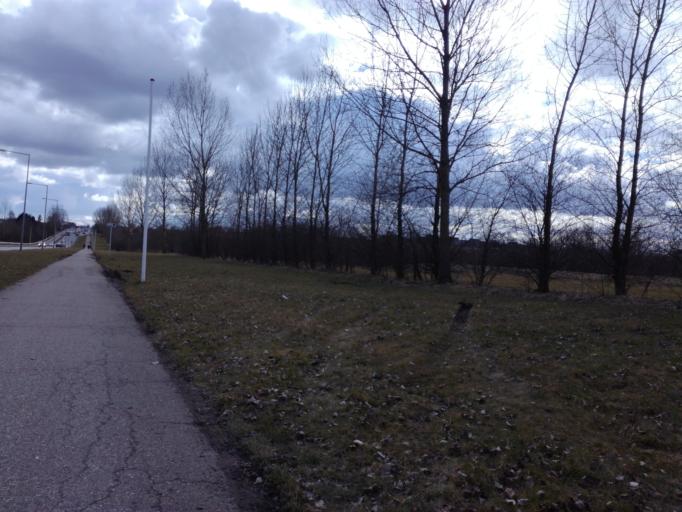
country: DK
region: South Denmark
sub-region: Fredericia Kommune
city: Fredericia
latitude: 55.5770
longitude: 9.7253
